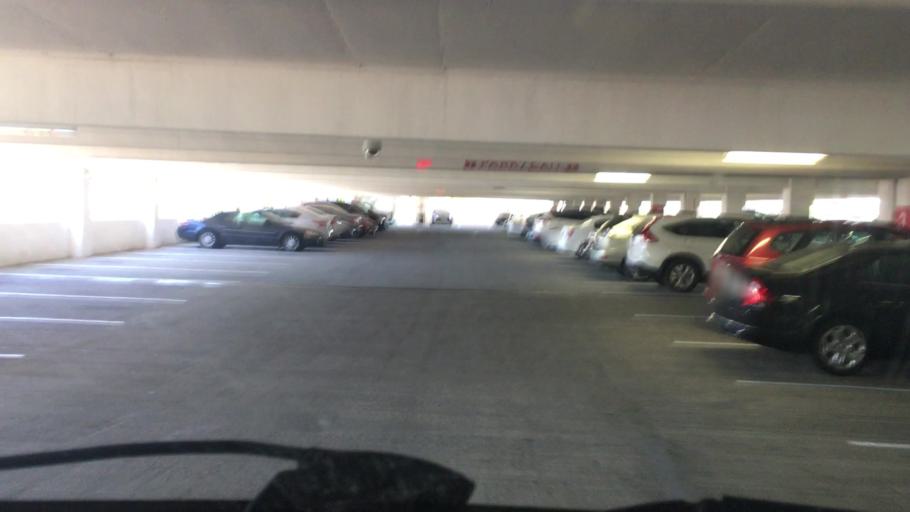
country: US
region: Maryland
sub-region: Prince George's County
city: College Park
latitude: 38.9952
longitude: -76.9436
